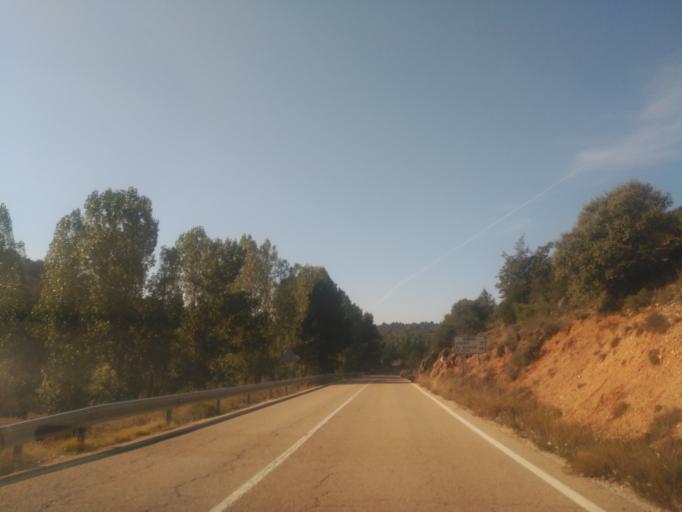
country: ES
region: Castille and Leon
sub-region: Provincia de Soria
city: Casarejos
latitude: 41.7918
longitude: -3.0296
